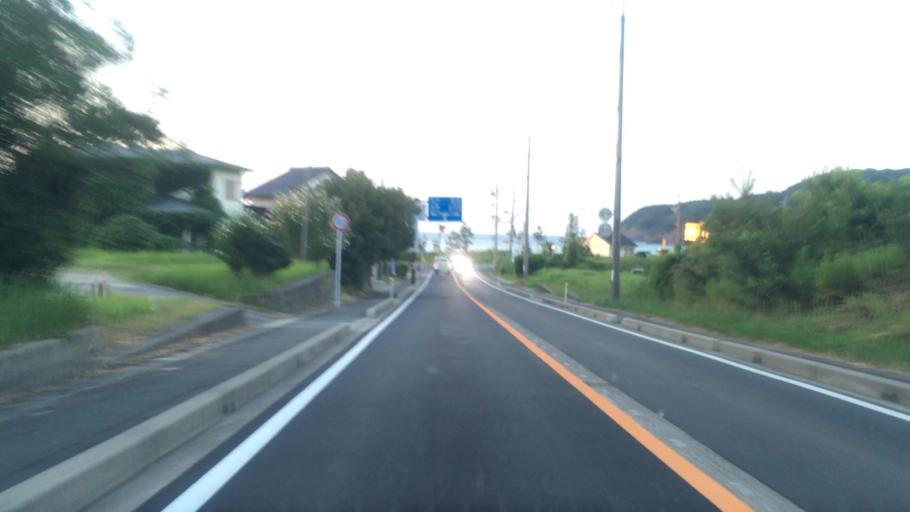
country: JP
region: Tottori
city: Tottori
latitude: 35.5896
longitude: 134.3327
